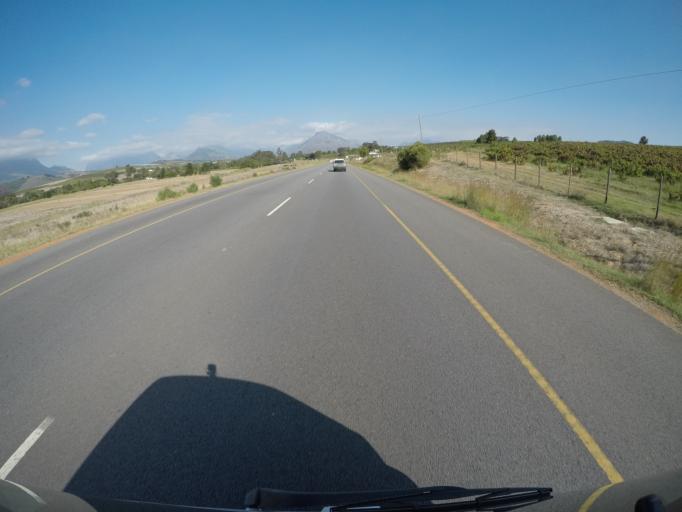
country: ZA
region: Western Cape
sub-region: Cape Winelands District Municipality
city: Stellenbosch
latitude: -33.8874
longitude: 18.8224
